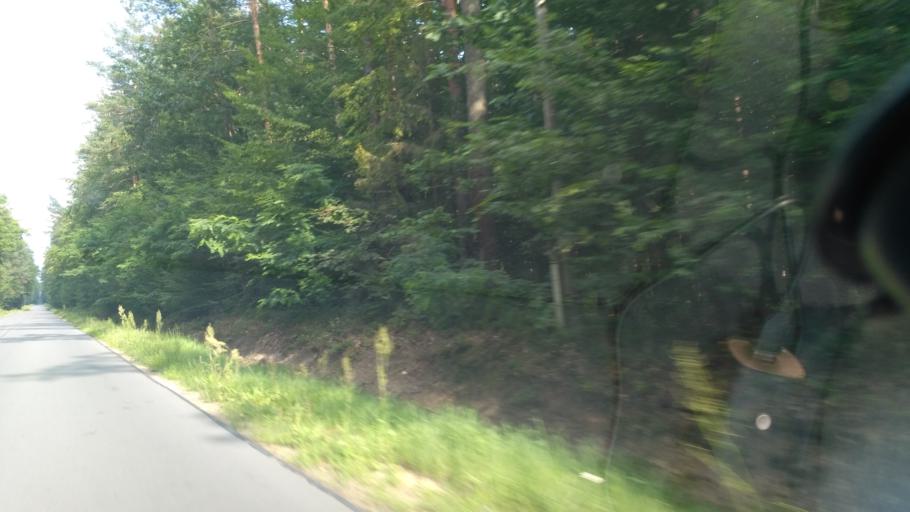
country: PL
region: Subcarpathian Voivodeship
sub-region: Powiat rzeszowski
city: Glogow Malopolski
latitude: 50.1618
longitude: 21.9881
